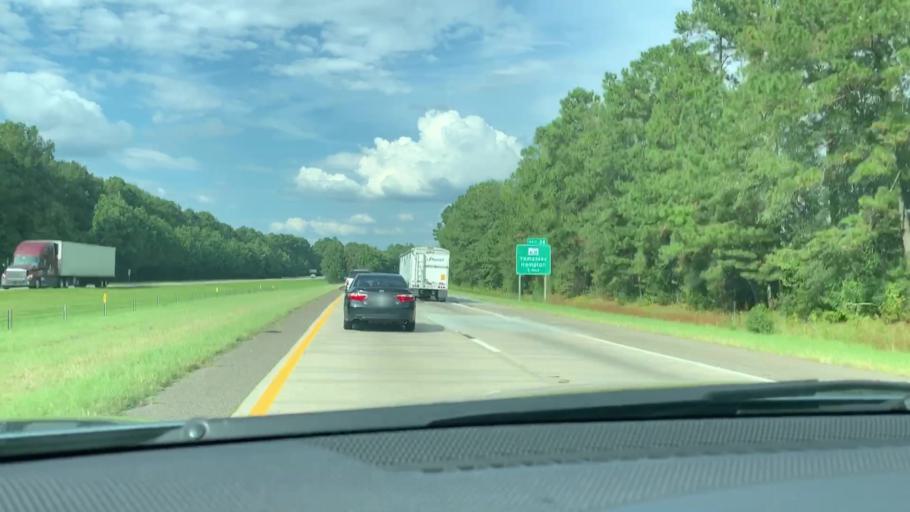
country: US
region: South Carolina
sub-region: Hampton County
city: Yemassee
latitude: 32.6871
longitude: -80.8809
